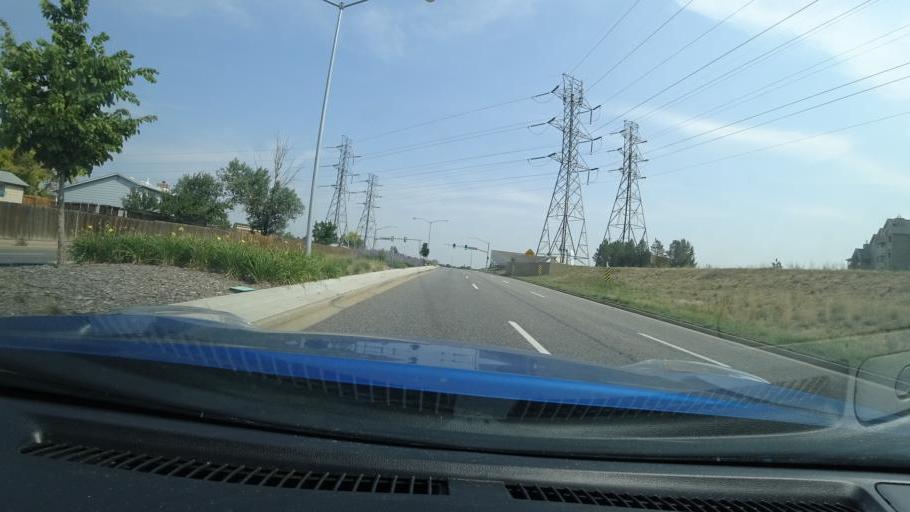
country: US
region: Colorado
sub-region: Adams County
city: Aurora
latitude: 39.6811
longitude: -104.7724
